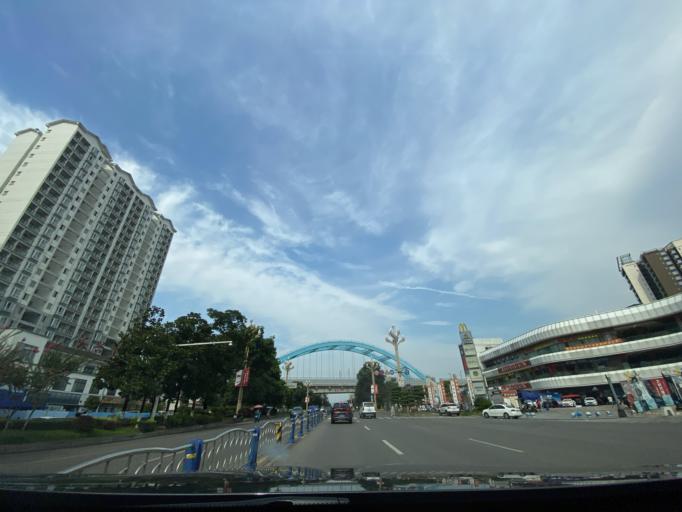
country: CN
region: Sichuan
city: Fuji
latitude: 29.1525
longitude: 105.3549
